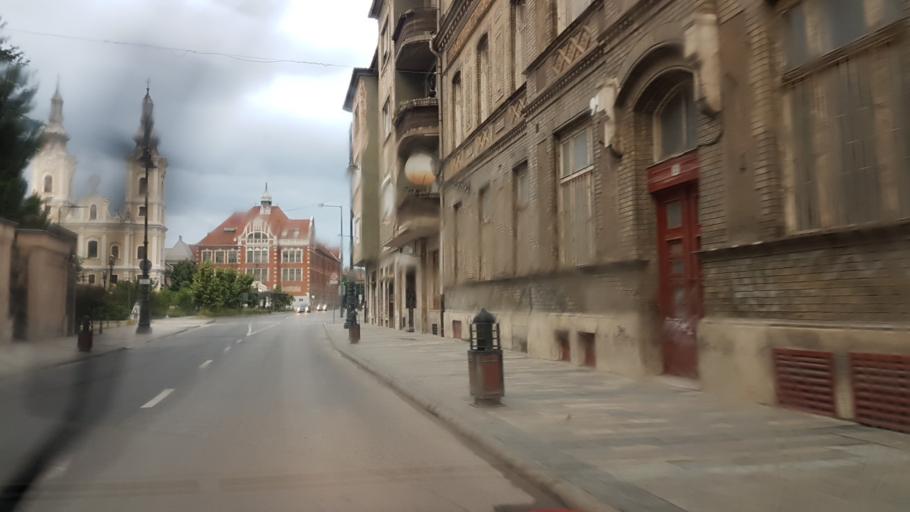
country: HU
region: Borsod-Abauj-Zemplen
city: Miskolc
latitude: 48.1038
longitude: 20.7854
